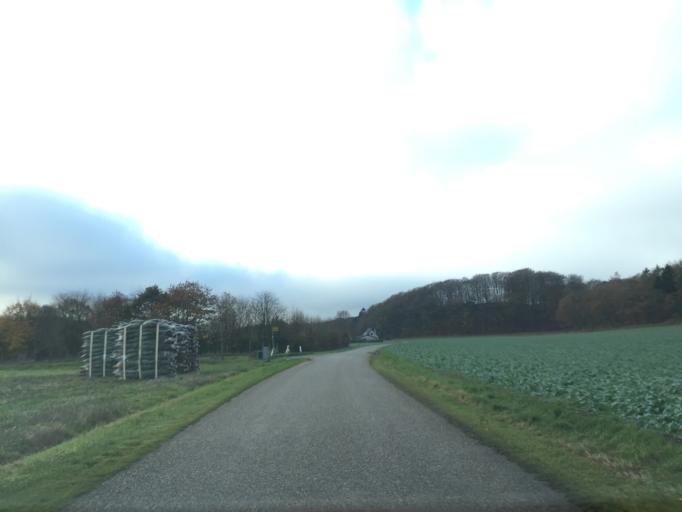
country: DK
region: Central Jutland
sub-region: Skanderborg Kommune
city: Ry
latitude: 56.1582
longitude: 9.7429
